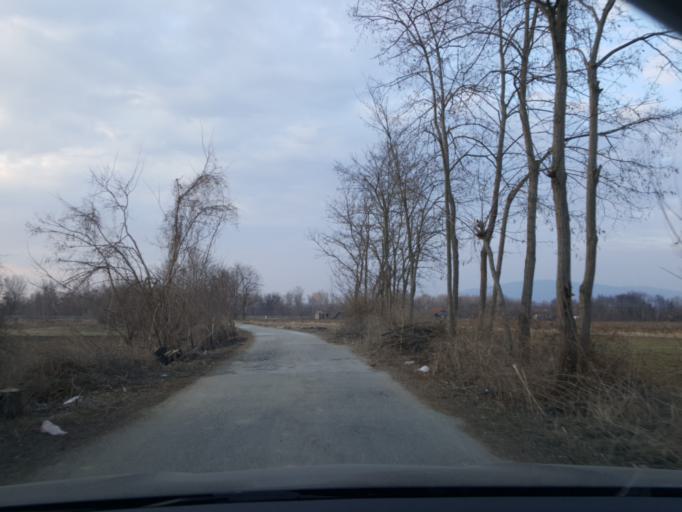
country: RS
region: Central Serbia
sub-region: Nisavski Okrug
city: Aleksinac
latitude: 43.5682
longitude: 21.6429
